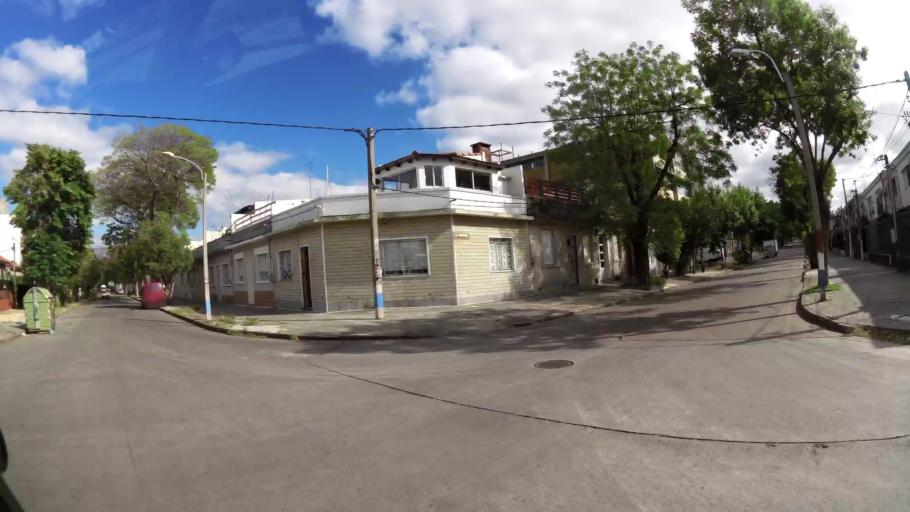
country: UY
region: Montevideo
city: Montevideo
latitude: -34.8782
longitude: -56.1628
